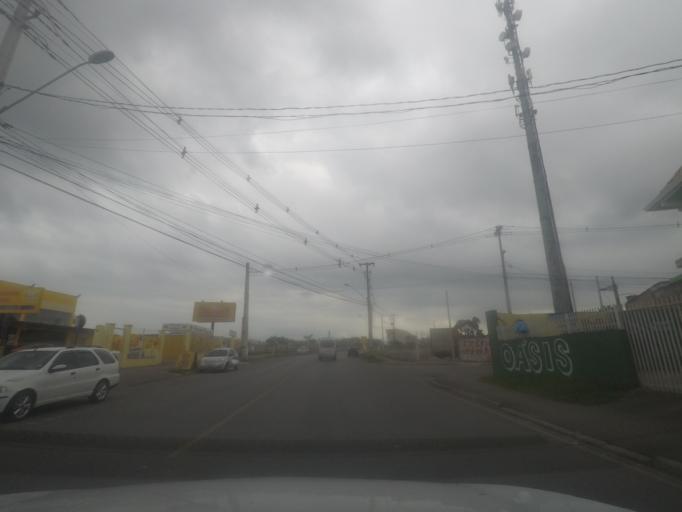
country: BR
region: Parana
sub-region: Sao Jose Dos Pinhais
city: Sao Jose dos Pinhais
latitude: -25.5578
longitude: -49.2555
